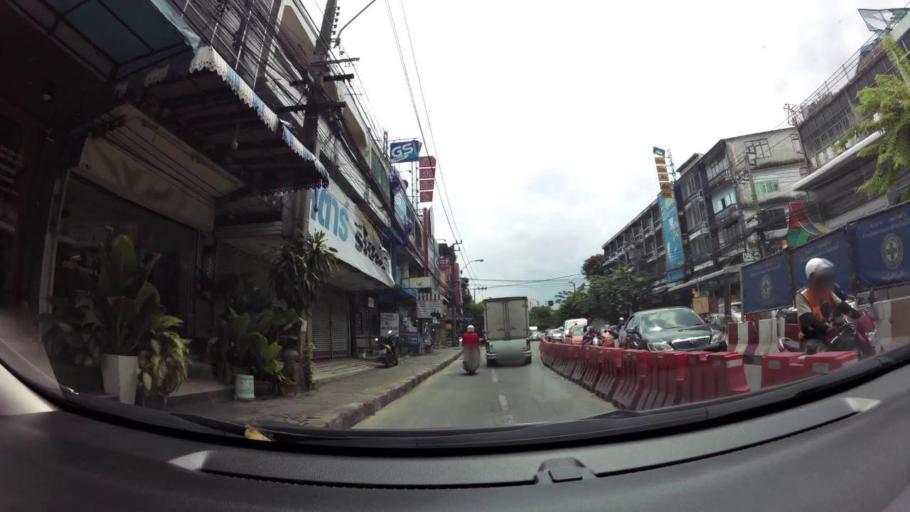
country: TH
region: Bangkok
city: Bang Na
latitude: 13.6782
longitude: 100.6279
